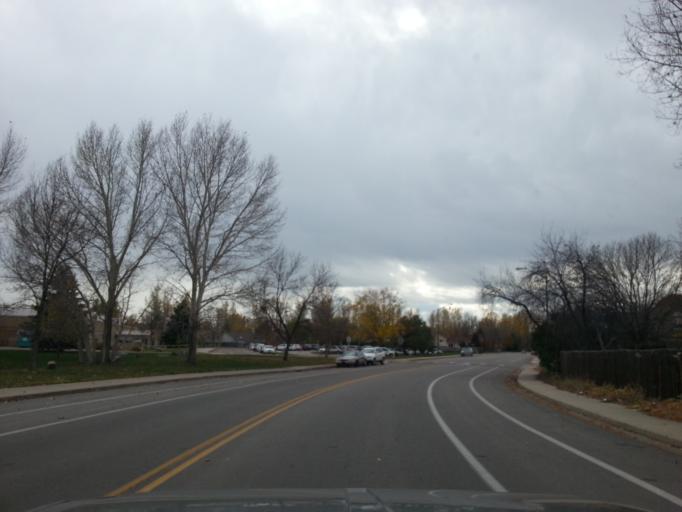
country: US
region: Colorado
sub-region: Larimer County
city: Fort Collins
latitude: 40.5337
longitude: -105.0321
